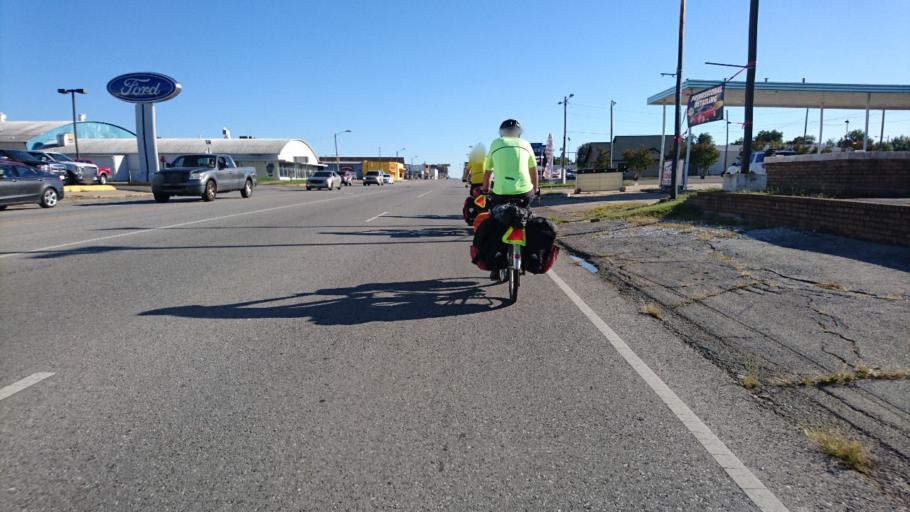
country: US
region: Oklahoma
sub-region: Ottawa County
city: Miami
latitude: 36.8823
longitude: -94.8776
